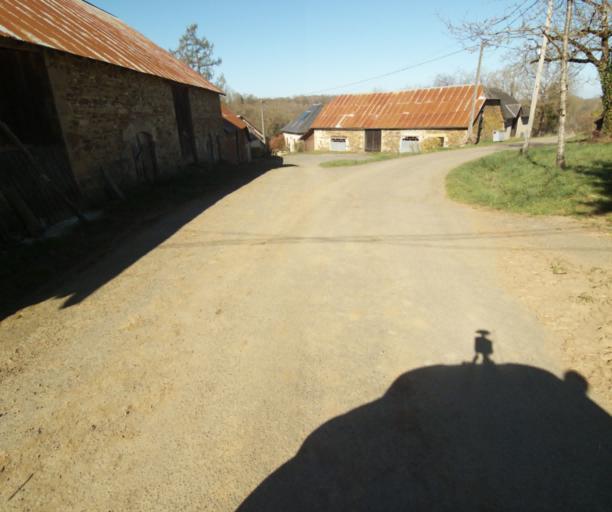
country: FR
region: Limousin
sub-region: Departement de la Correze
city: Seilhac
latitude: 45.4038
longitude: 1.7450
